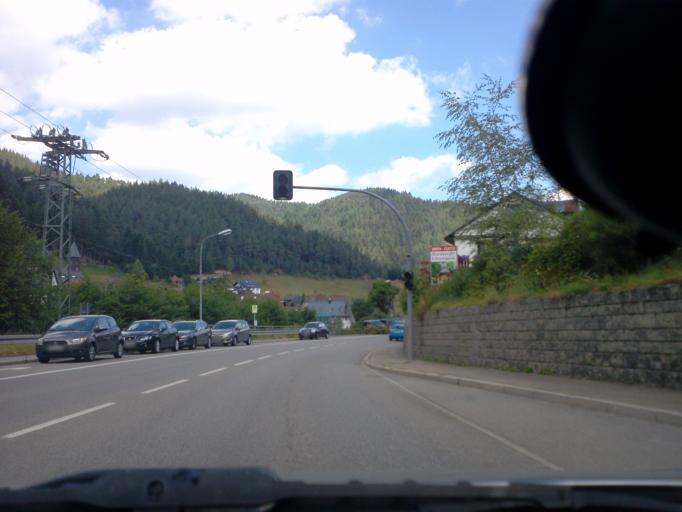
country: DE
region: Baden-Wuerttemberg
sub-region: Freiburg Region
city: Hornberg
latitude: 48.1875
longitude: 8.2306
